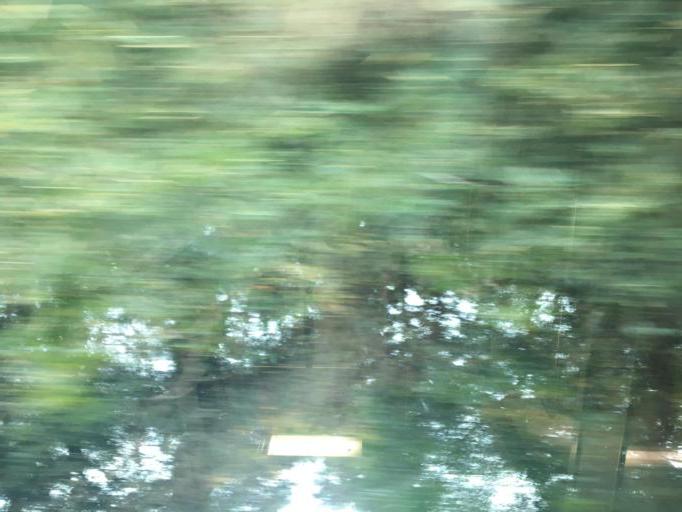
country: JP
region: Ibaraki
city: Kasama
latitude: 36.3665
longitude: 140.2561
